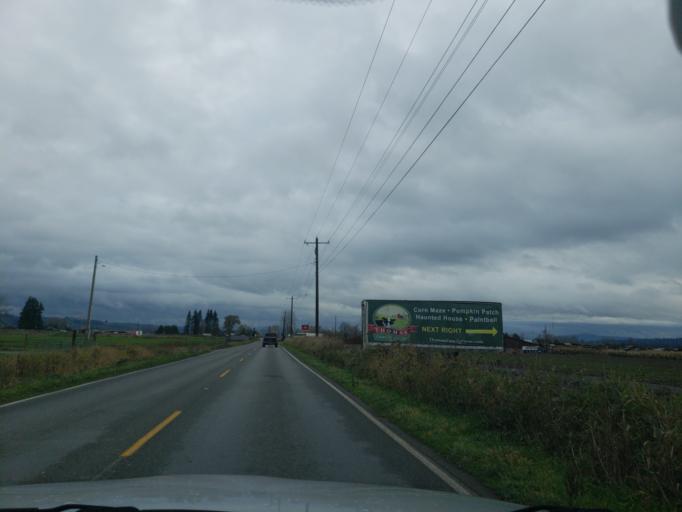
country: US
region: Washington
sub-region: Snohomish County
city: Snohomish
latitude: 47.8990
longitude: -122.1156
